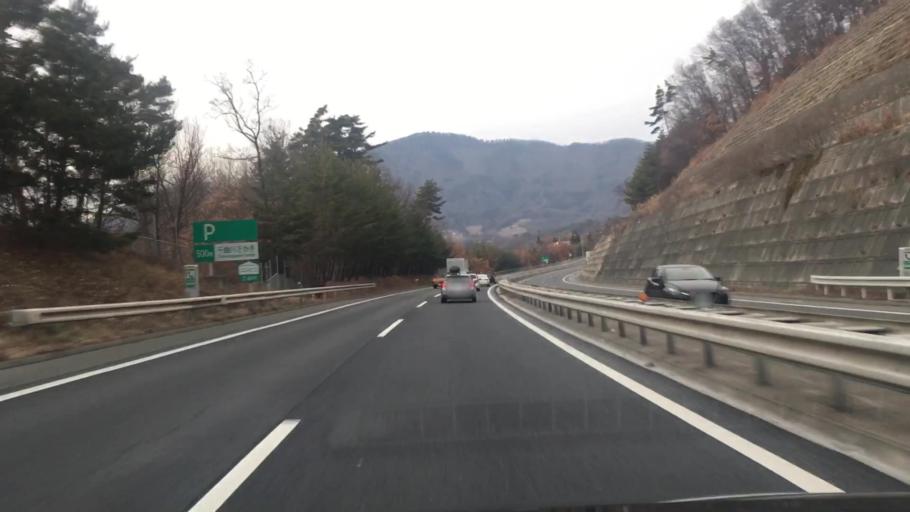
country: JP
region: Nagano
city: Ueda
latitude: 36.4495
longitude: 138.2023
